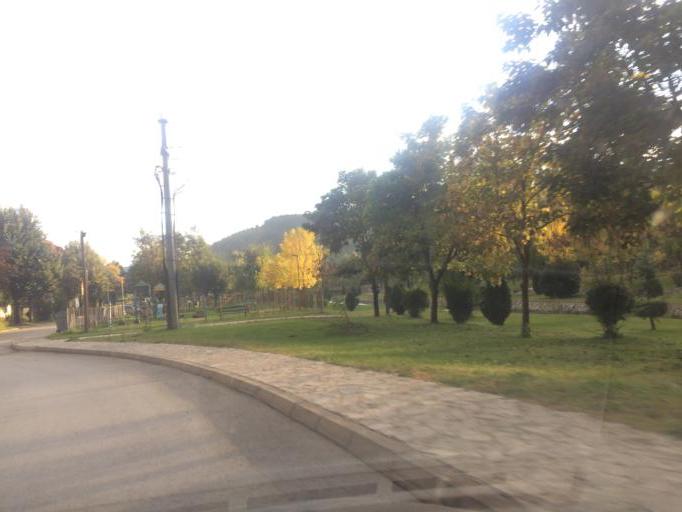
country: MK
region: Makedonska Kamenica
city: Makedonska Kamenica
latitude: 42.0212
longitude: 22.5878
